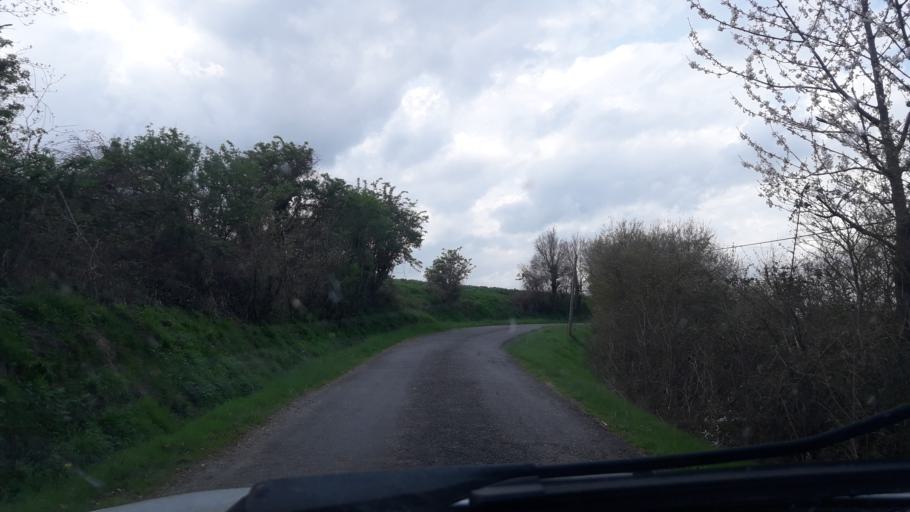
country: FR
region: Midi-Pyrenees
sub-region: Departement de l'Ariege
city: Lezat-sur-Leze
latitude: 43.1914
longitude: 1.3296
